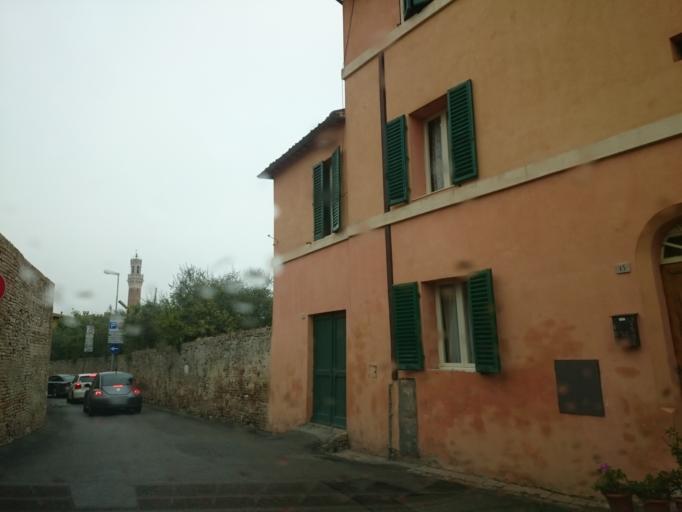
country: IT
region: Tuscany
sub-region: Provincia di Siena
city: Siena
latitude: 43.3140
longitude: 11.3337
